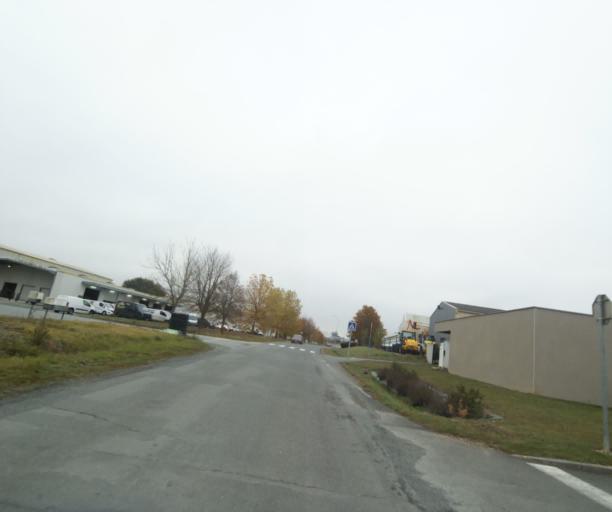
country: FR
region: Poitou-Charentes
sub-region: Departement de la Charente-Maritime
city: Saintes
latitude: 45.7524
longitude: -0.6681
